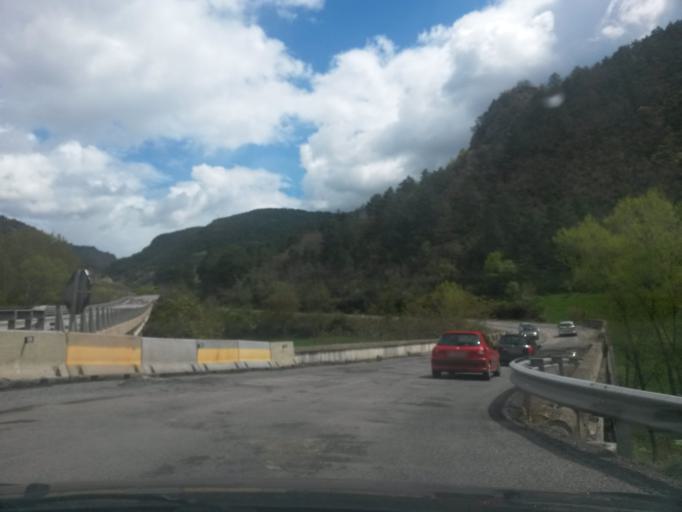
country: ES
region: Catalonia
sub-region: Provincia de Lleida
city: el Pont de Bar
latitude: 42.3711
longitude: 1.6045
